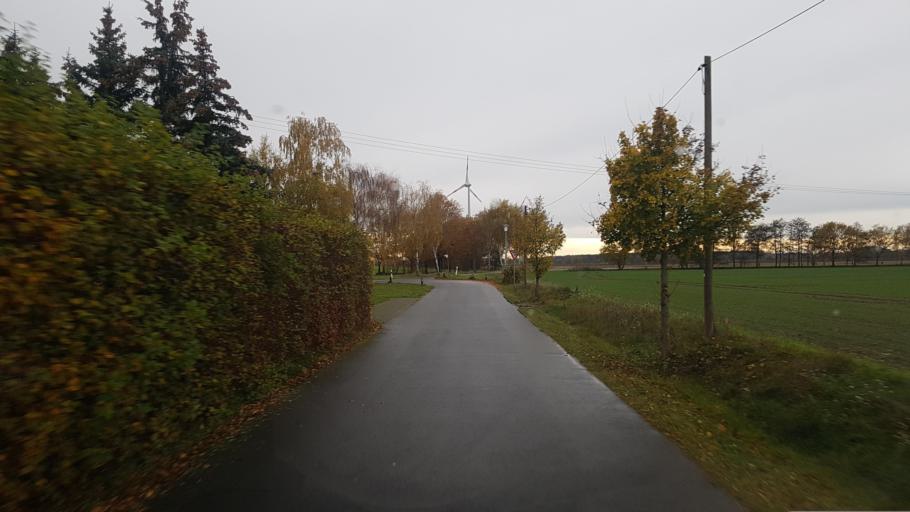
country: DE
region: Saxony-Anhalt
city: Muhlanger
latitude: 51.8730
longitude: 12.7490
